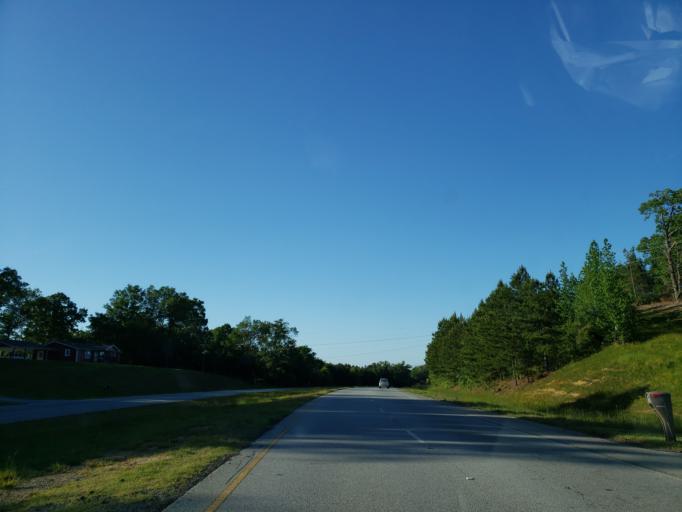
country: US
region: Georgia
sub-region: Polk County
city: Cedartown
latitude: 33.9356
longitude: -85.2467
